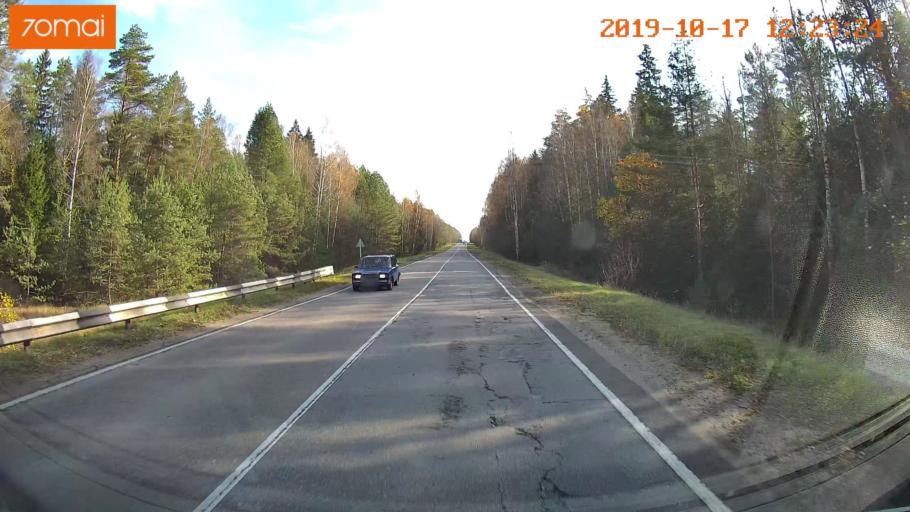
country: RU
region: Rjazan
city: Gus'-Zheleznyy
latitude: 55.0444
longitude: 41.1926
